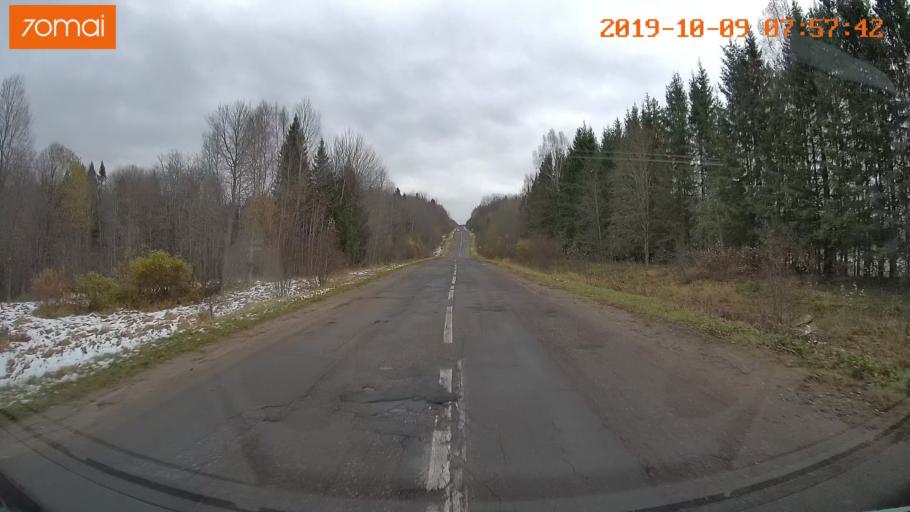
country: RU
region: Jaroslavl
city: Kukoboy
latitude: 58.6970
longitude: 39.9545
